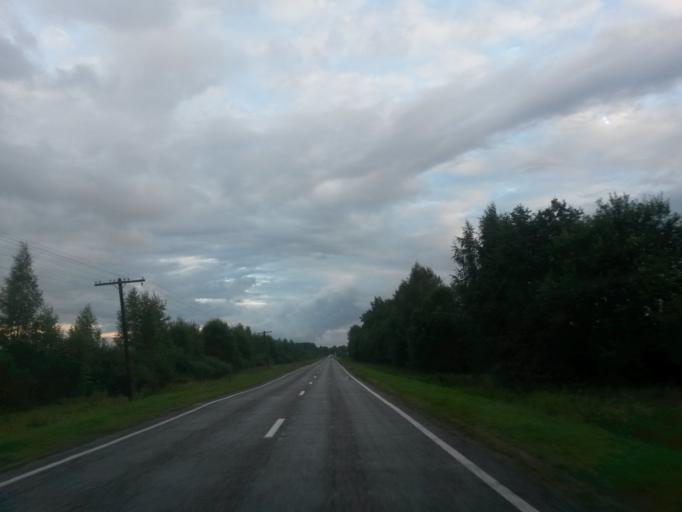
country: RU
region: Jaroslavl
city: Tutayev
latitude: 57.9083
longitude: 39.5198
